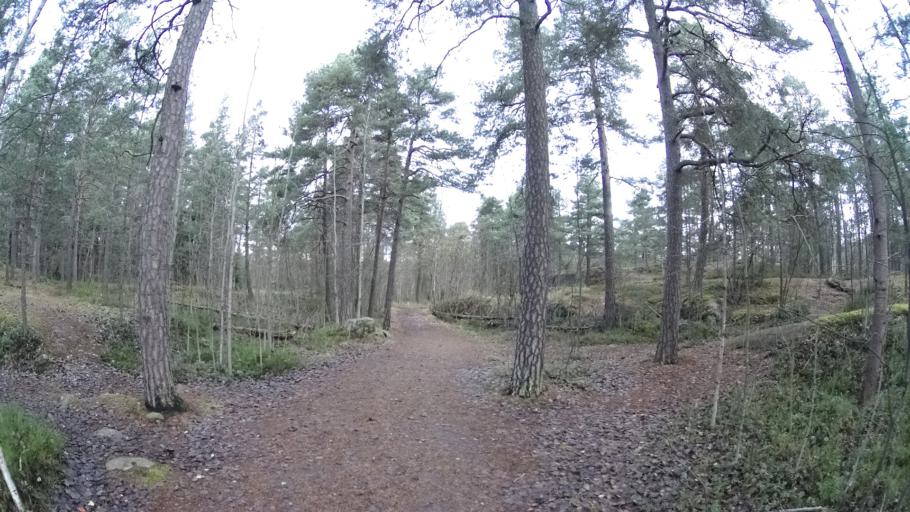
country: FI
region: Uusimaa
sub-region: Helsinki
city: Helsinki
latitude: 60.1960
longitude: 24.9130
